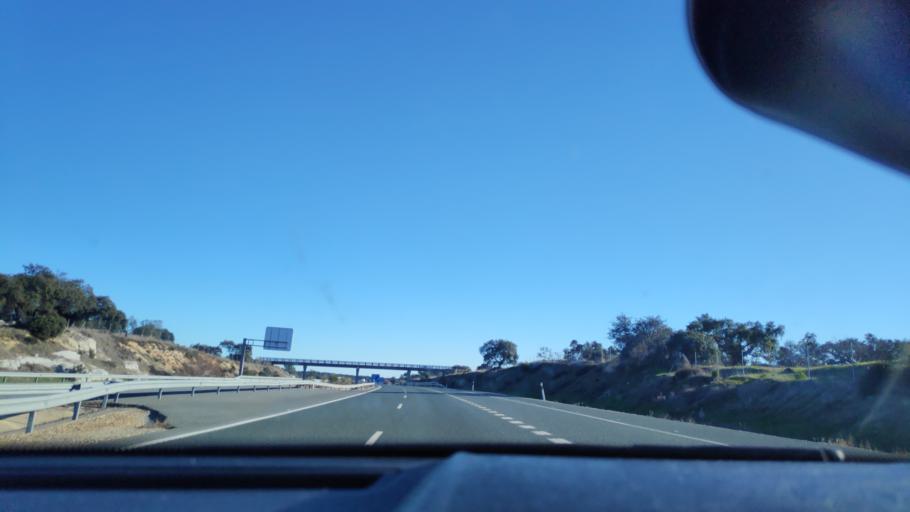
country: ES
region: Andalusia
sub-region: Provincia de Huelva
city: Santa Olalla del Cala
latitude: 37.9177
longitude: -6.2231
